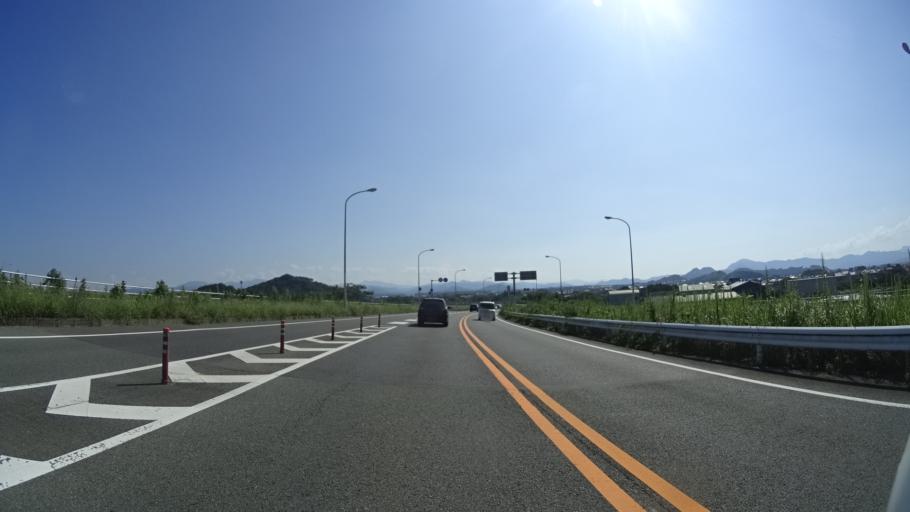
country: JP
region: Fukuoka
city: Yukuhashi
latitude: 33.7047
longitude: 130.9979
